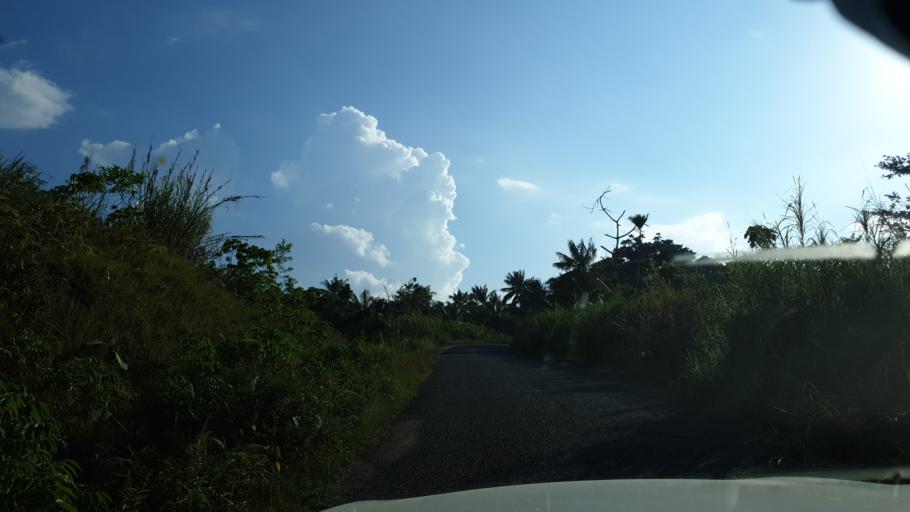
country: PG
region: East Sepik
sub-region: Wewak
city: Wewak
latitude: -3.6955
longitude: 143.6509
